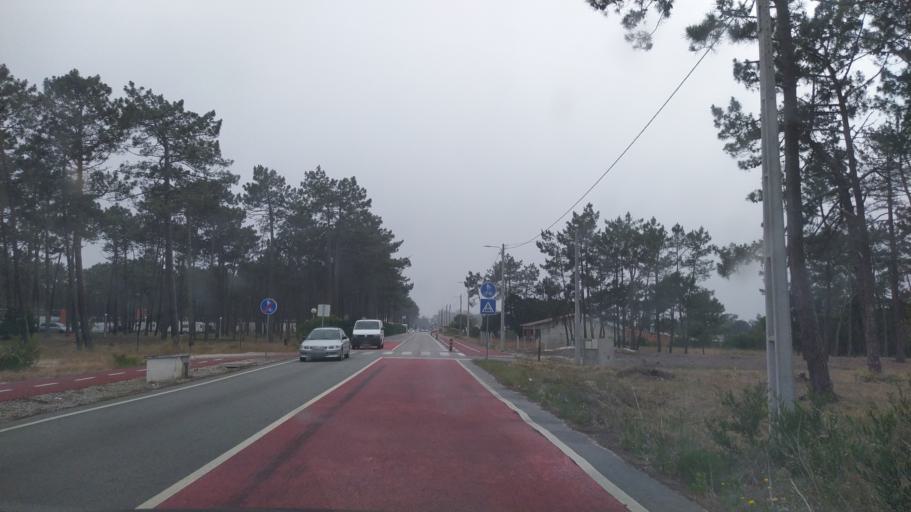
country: PT
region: Aveiro
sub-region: Ilhavo
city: Gafanha da Encarnacao
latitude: 40.5605
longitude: -8.7437
